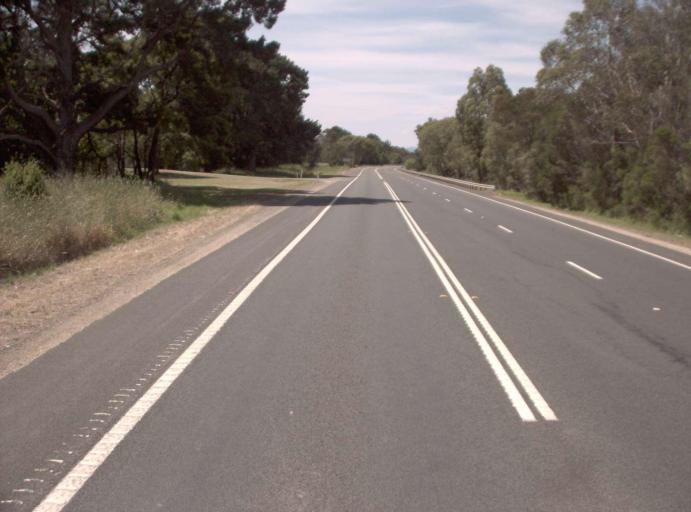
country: AU
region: Victoria
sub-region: Wellington
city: Sale
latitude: -37.9936
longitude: 147.0653
